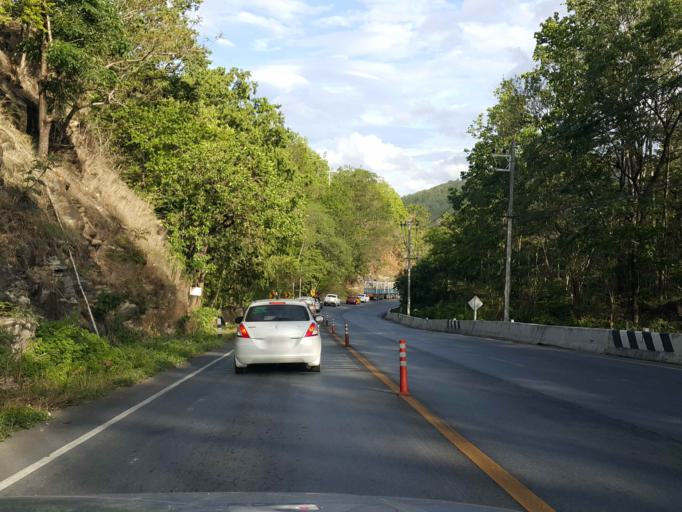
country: TH
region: Tak
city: Tak
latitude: 16.8128
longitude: 98.9775
